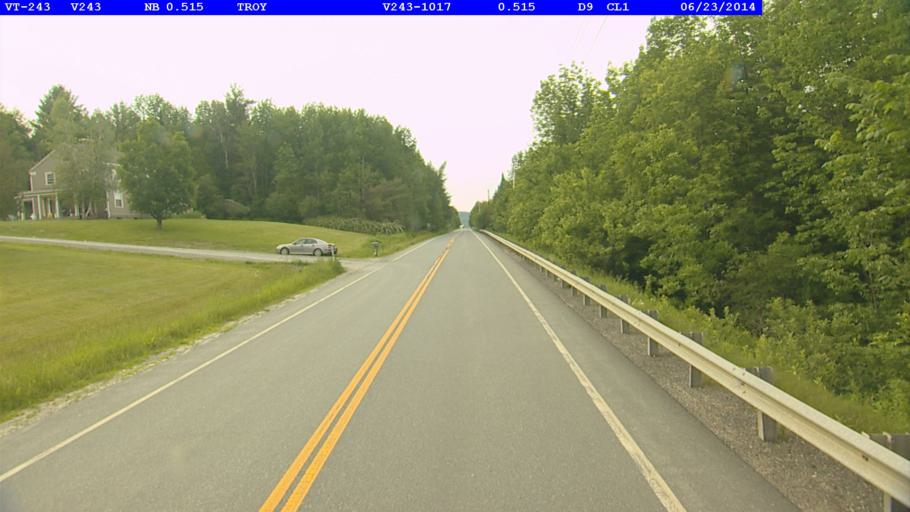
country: US
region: Vermont
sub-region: Orleans County
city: Newport
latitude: 45.0003
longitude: -72.4117
